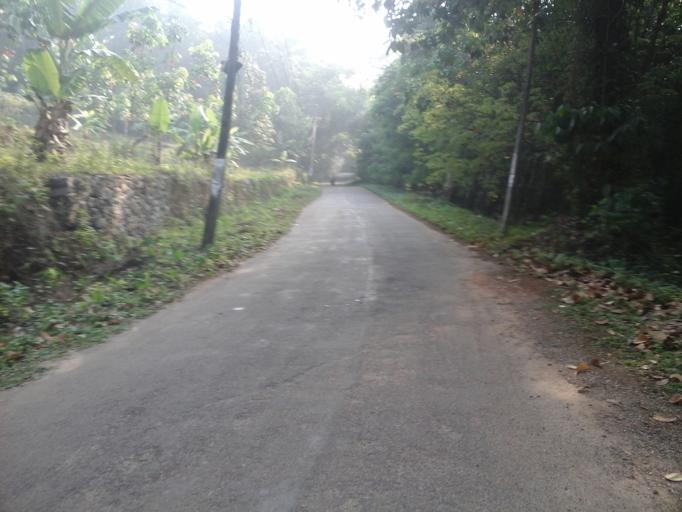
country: IN
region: Kerala
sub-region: Kottayam
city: Erattupetta
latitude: 9.5935
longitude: 76.7243
